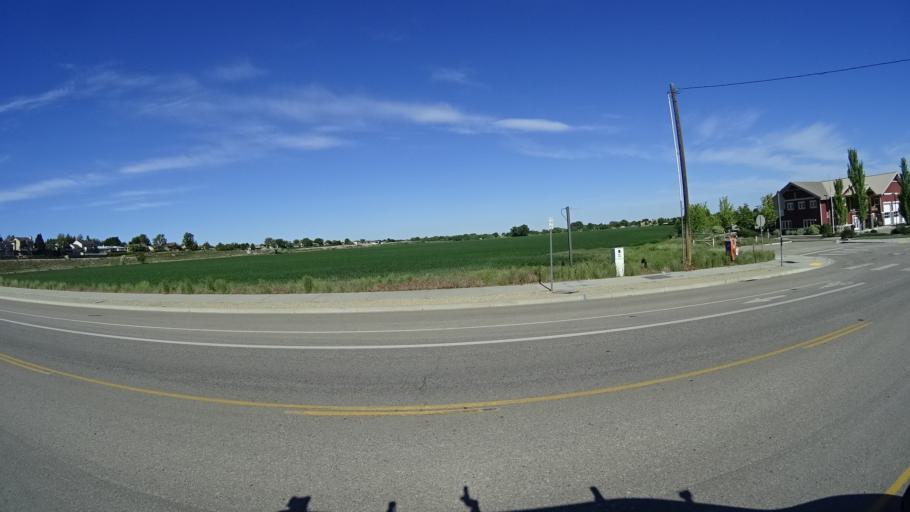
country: US
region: Idaho
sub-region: Ada County
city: Garden City
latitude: 43.5662
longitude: -116.2741
